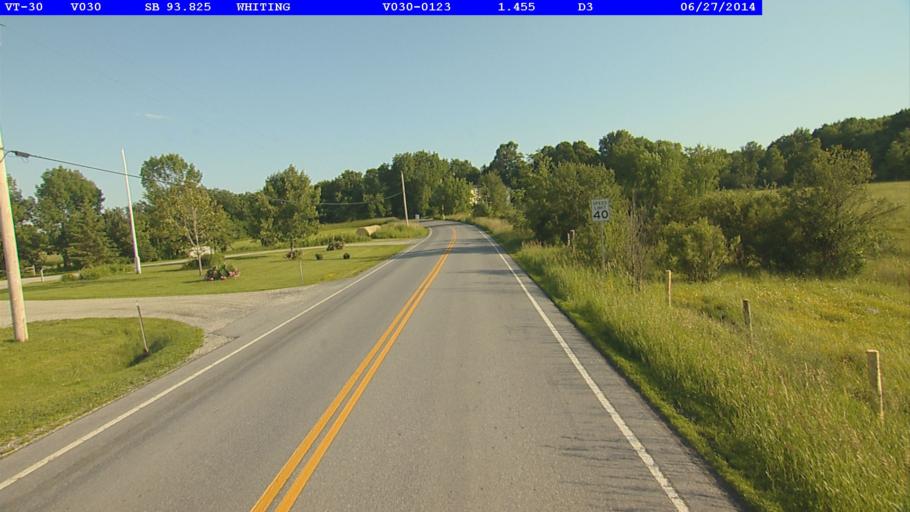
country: US
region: Vermont
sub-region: Rutland County
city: Brandon
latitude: 43.8584
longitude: -73.2021
